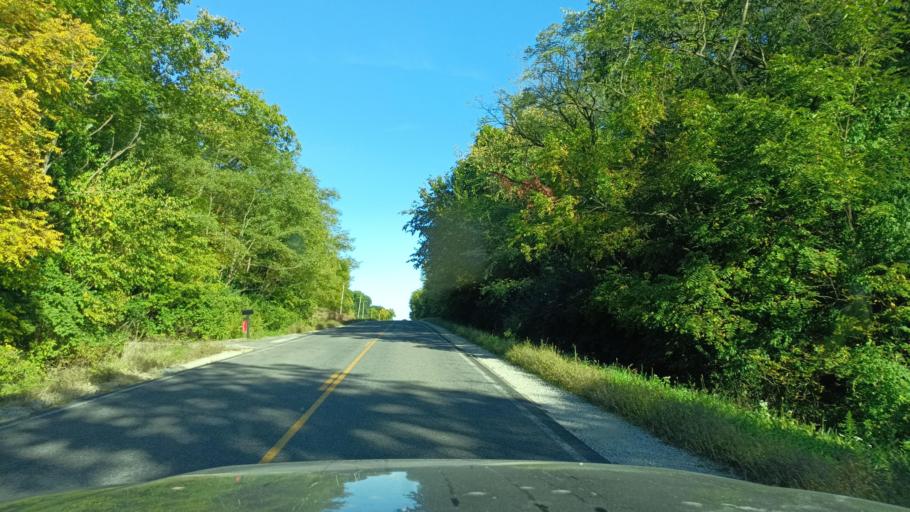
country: US
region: Illinois
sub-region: McLean County
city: Le Roy
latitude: 40.2244
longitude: -88.8174
